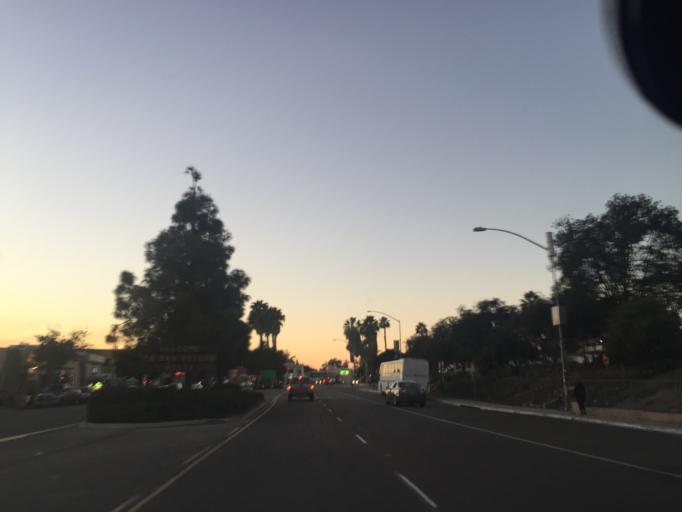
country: MX
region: Baja California
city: Tijuana
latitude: 32.5467
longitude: -117.0323
